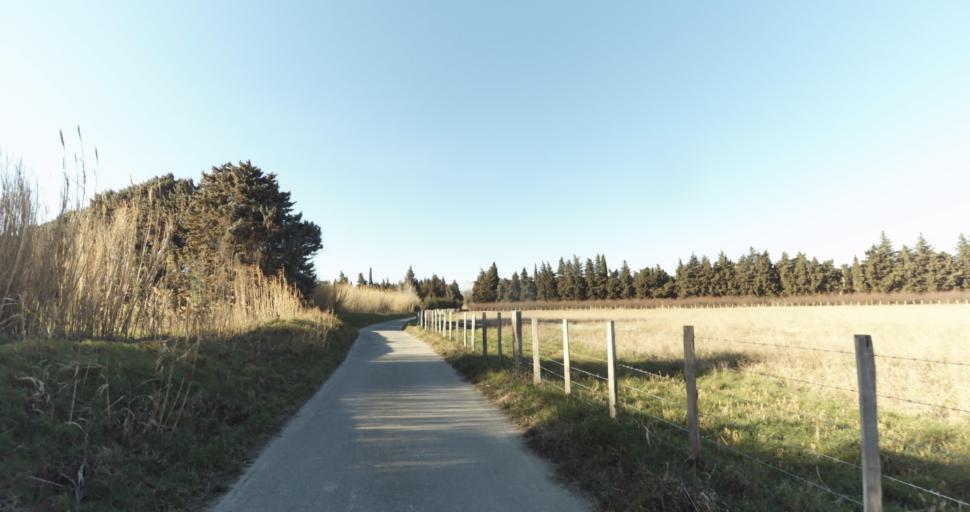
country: FR
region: Provence-Alpes-Cote d'Azur
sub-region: Departement des Bouches-du-Rhone
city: Barbentane
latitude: 43.9153
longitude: 4.7548
